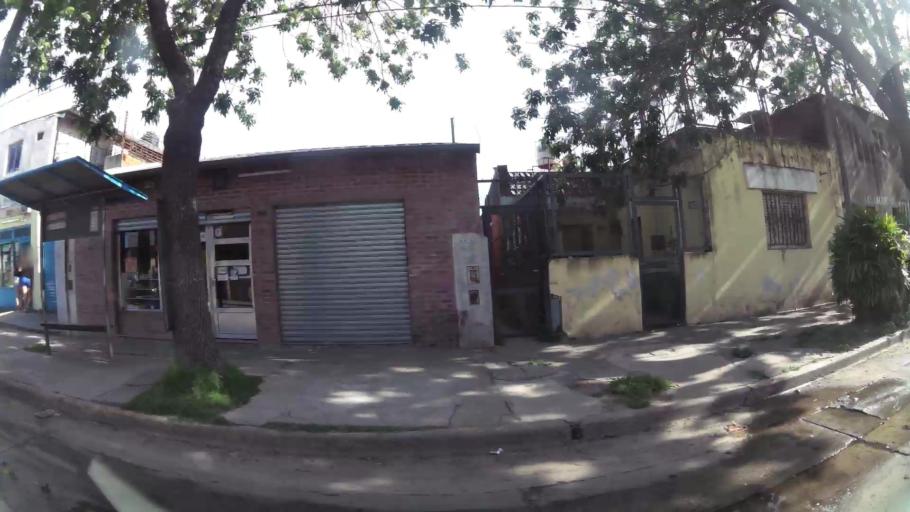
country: AR
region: Santa Fe
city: Granadero Baigorria
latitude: -32.9157
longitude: -60.6992
